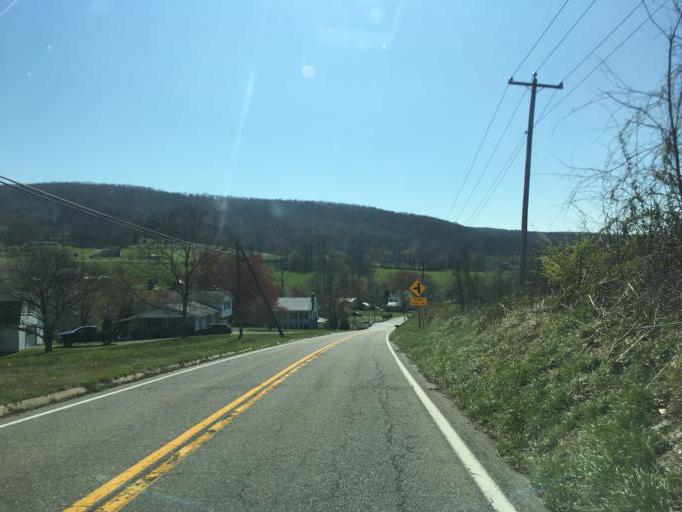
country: US
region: Maryland
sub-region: Frederick County
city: Myersville
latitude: 39.5640
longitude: -77.5270
